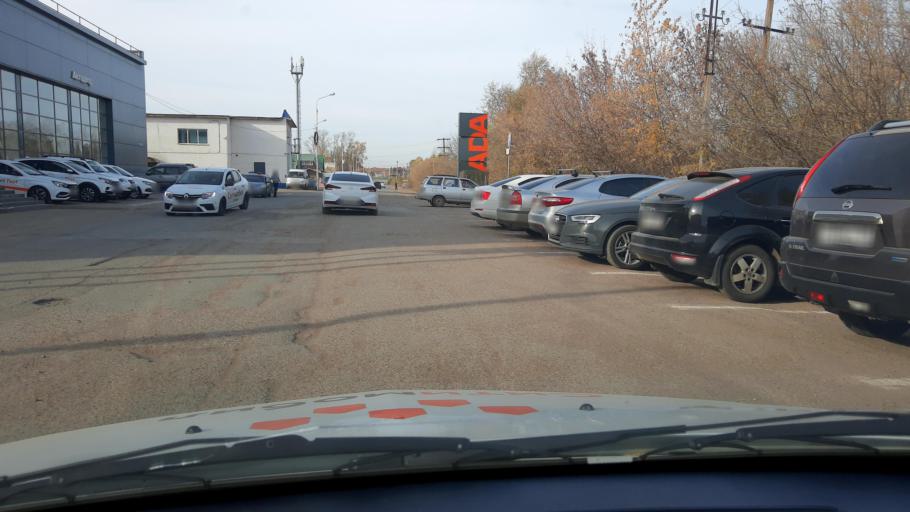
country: RU
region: Bashkortostan
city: Ufa
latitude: 54.7690
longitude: 55.9620
